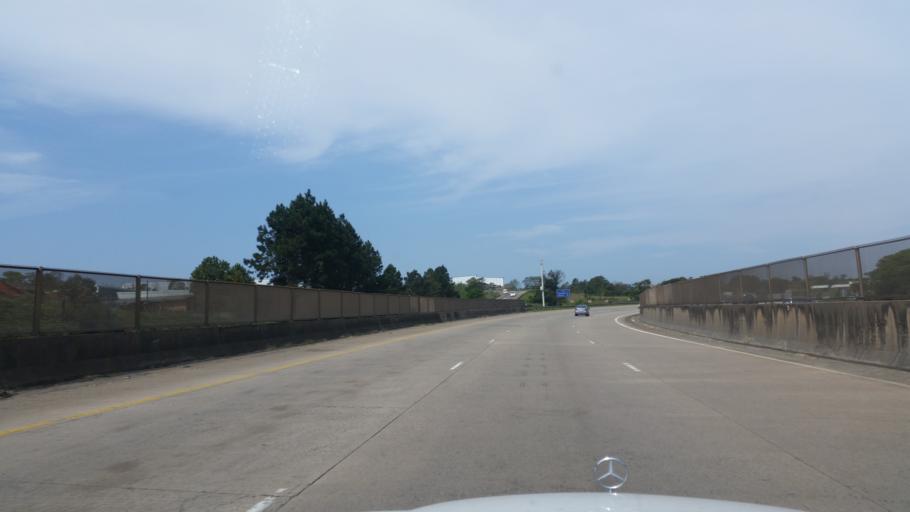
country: ZA
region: KwaZulu-Natal
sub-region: uMgungundlovu District Municipality
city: Camperdown
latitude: -29.7320
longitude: 30.5962
